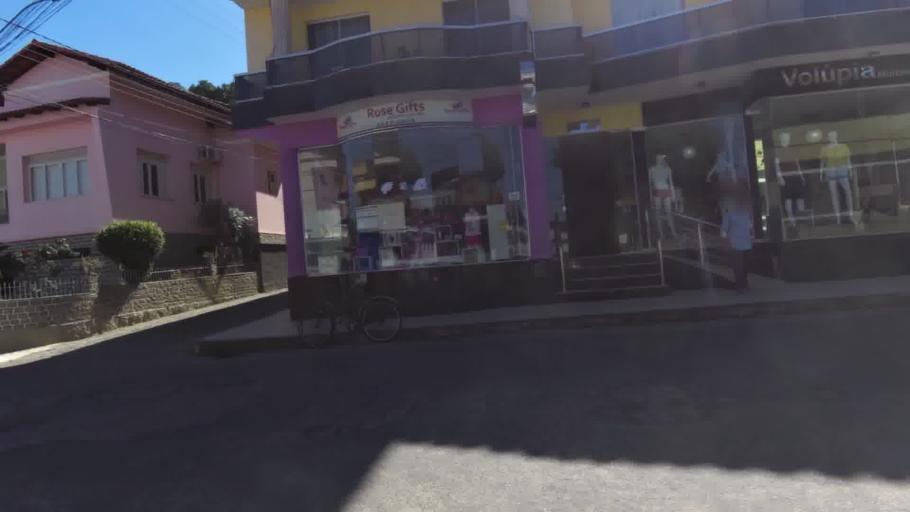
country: BR
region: Espirito Santo
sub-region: Rio Novo Do Sul
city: Rio Novo do Sul
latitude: -20.8619
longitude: -40.9347
